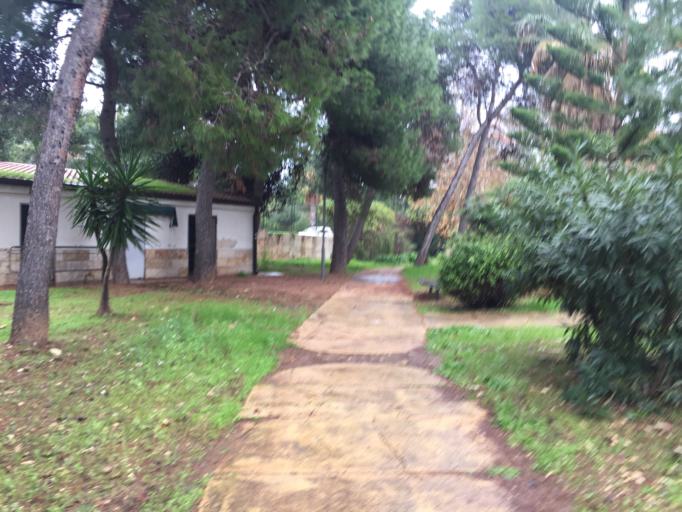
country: IT
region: Apulia
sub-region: Provincia di Bari
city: Bari
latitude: 41.1324
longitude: 16.8305
